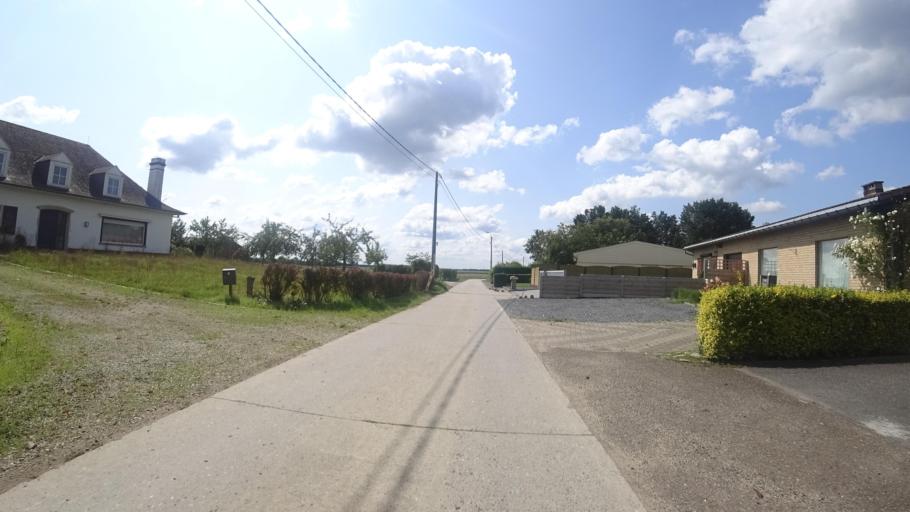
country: BE
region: Flanders
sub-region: Provincie Vlaams-Brabant
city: Huldenberg
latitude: 50.7791
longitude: 4.5922
